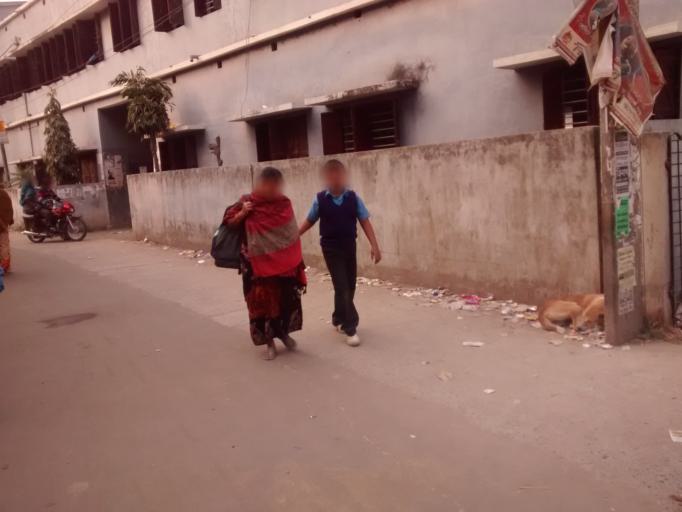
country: IN
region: West Bengal
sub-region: North 24 Parganas
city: Barasat
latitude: 22.7197
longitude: 88.4691
